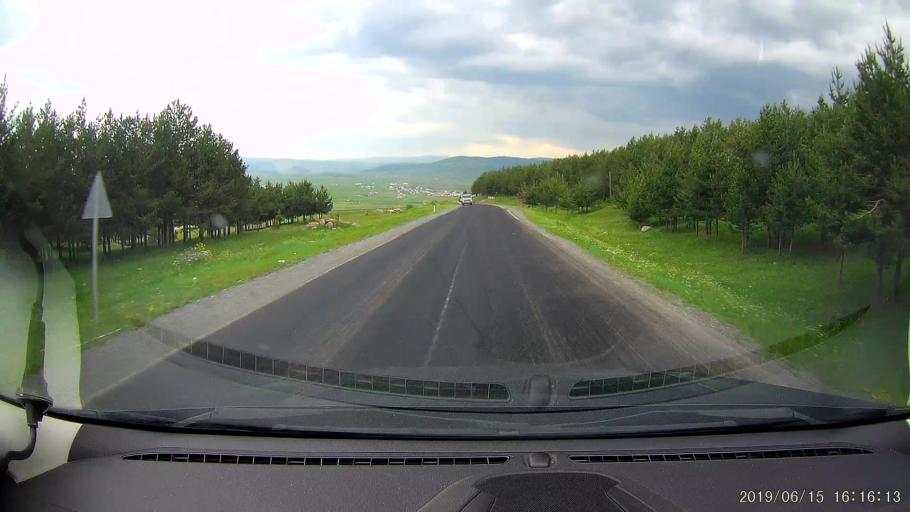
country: TR
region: Ardahan
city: Hanak
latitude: 41.2610
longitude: 42.8527
